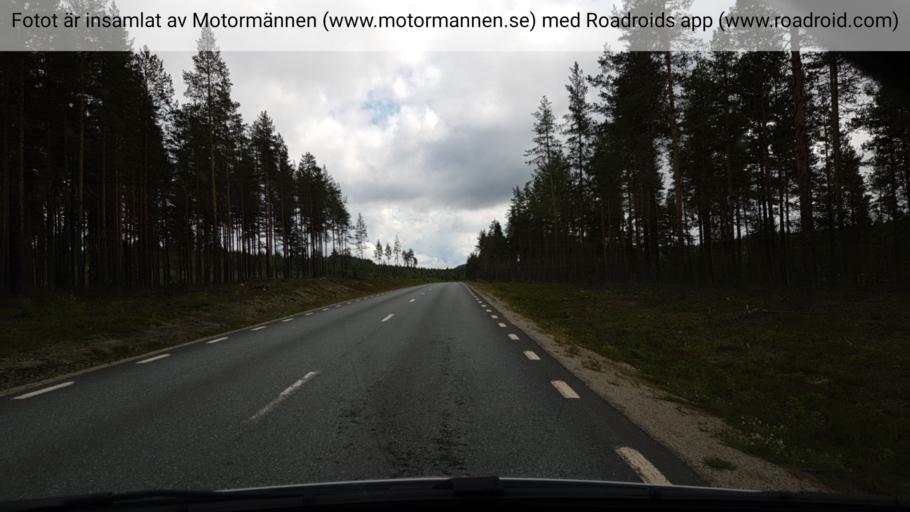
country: SE
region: Vaesterbotten
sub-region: Lycksele Kommun
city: Lycksele
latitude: 64.4152
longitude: 19.0137
